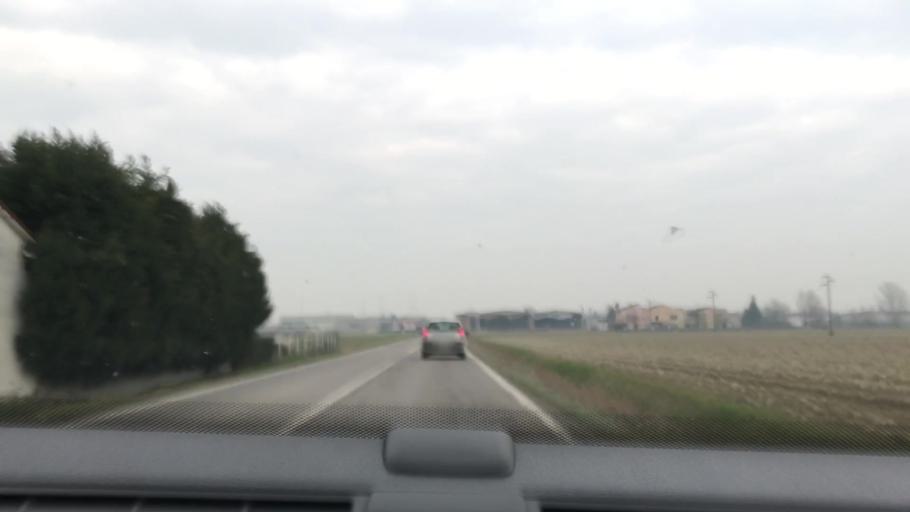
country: IT
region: Lombardy
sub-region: Provincia di Mantova
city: Dosolo
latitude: 44.9460
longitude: 10.6283
